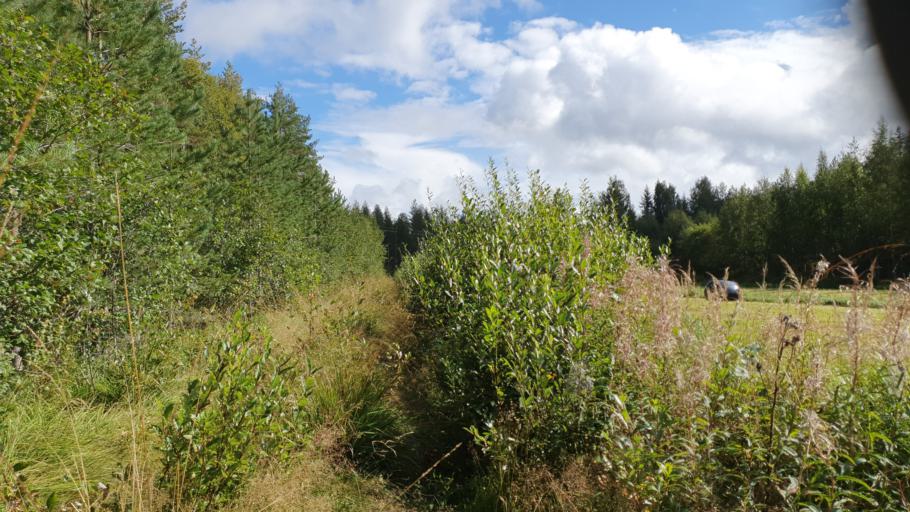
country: FI
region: Kainuu
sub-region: Kehys-Kainuu
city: Kuhmo
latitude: 64.1453
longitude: 29.3356
